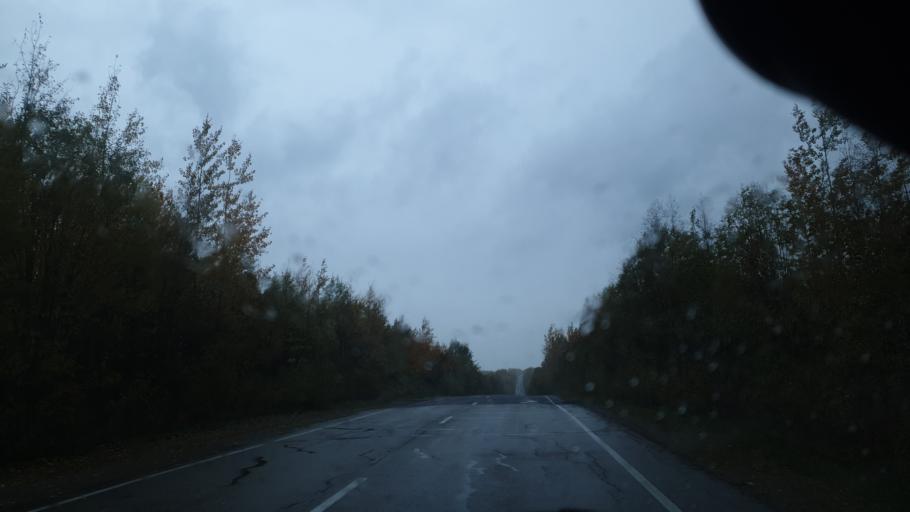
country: RU
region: Komi Republic
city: Nizhniy Odes
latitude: 63.6249
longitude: 55.1893
